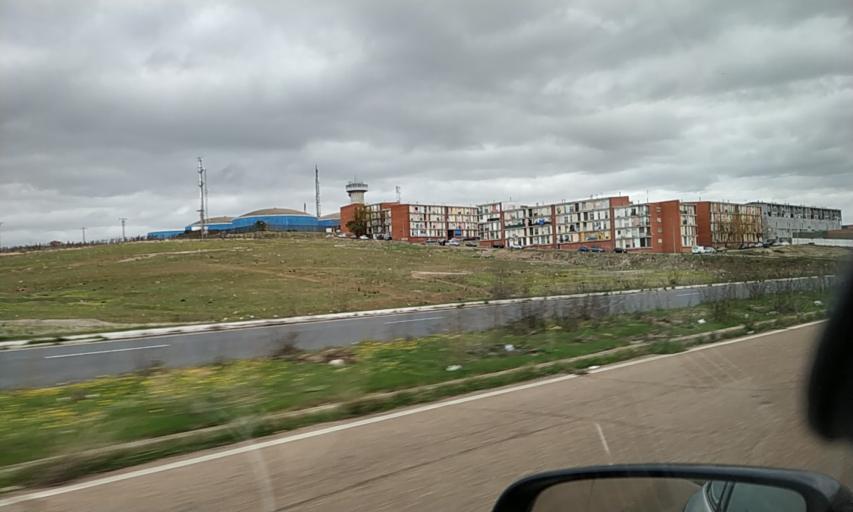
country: ES
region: Extremadura
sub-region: Provincia de Badajoz
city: Badajoz
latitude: 38.8986
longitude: -6.9867
